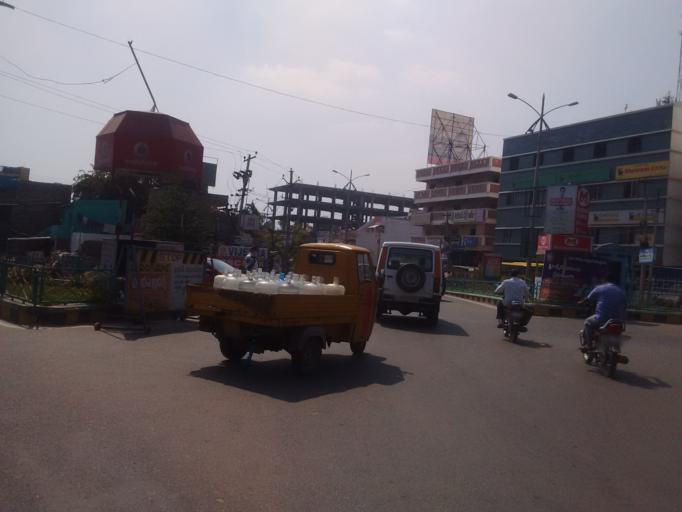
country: IN
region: Telangana
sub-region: Mahbubnagar
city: Alampur
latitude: 15.8121
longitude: 78.0405
